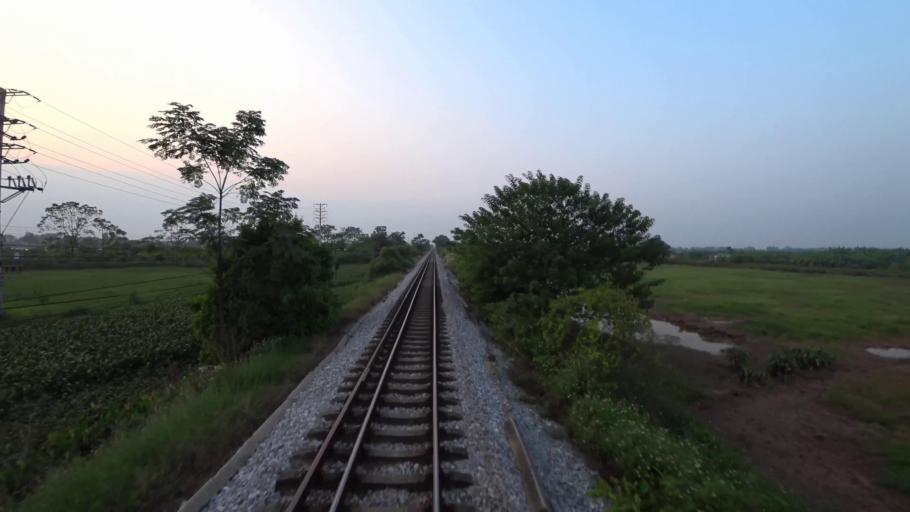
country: VN
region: Ha Noi
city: Dong Anh
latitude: 21.1227
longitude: 105.8839
